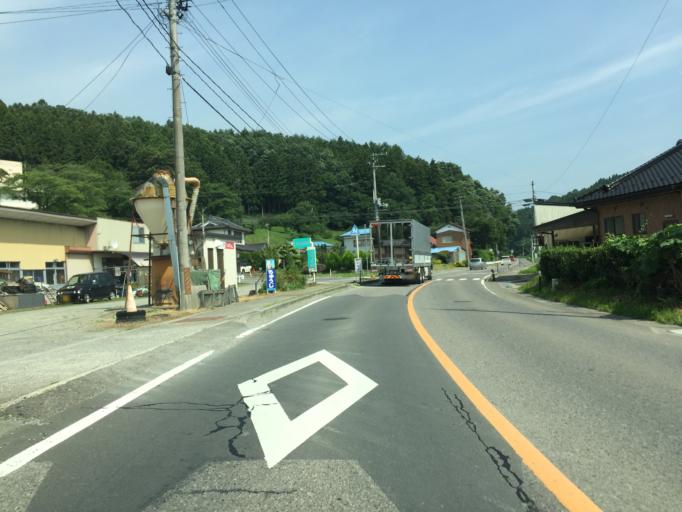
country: JP
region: Fukushima
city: Funehikimachi-funehiki
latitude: 37.4426
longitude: 140.6182
